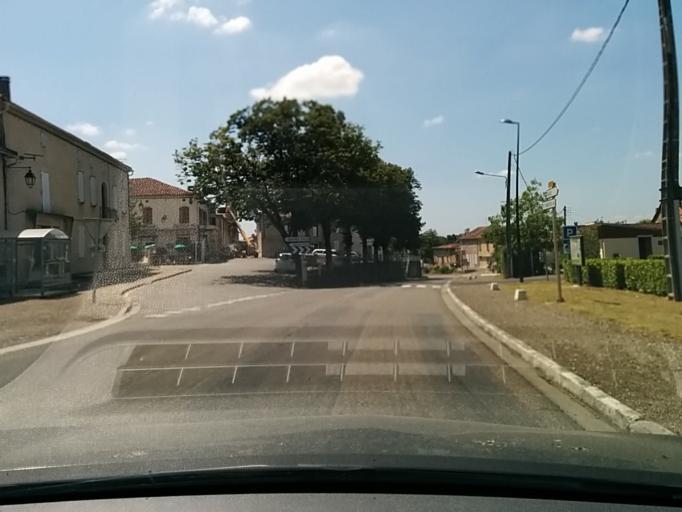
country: FR
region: Midi-Pyrenees
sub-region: Departement du Gers
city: Eauze
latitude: 43.8002
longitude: 0.0436
